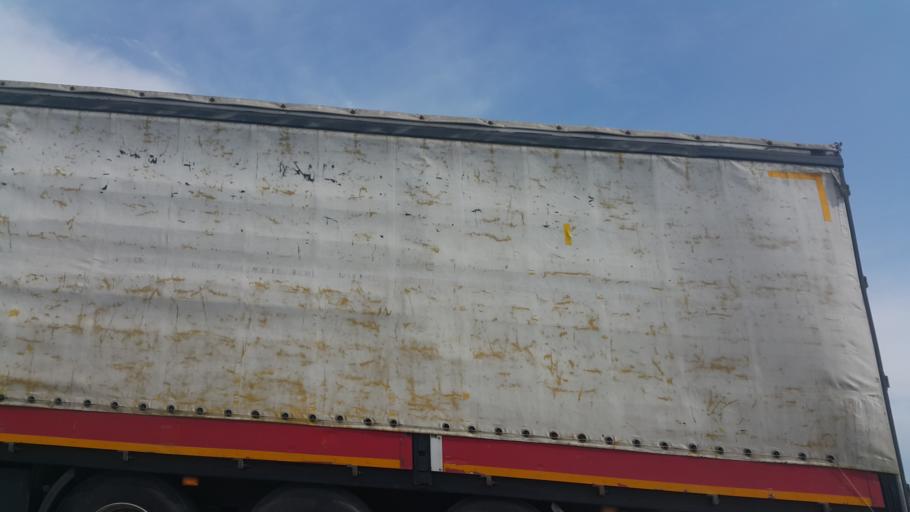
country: TR
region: Mersin
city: Mercin
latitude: 36.9007
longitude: 34.6624
